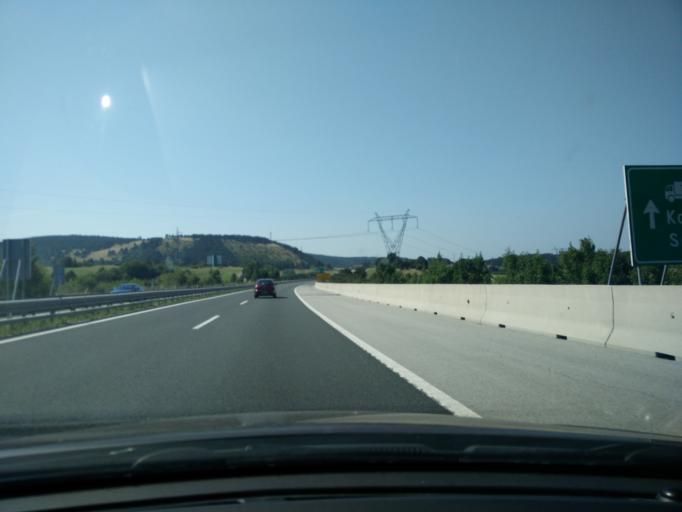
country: SI
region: Divaca
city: Divaca
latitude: 45.7256
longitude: 14.0147
